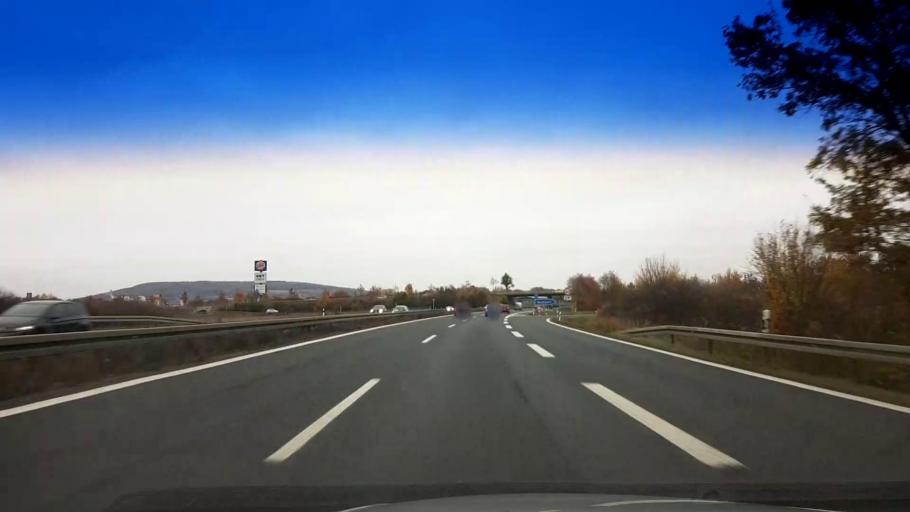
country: DE
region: Bavaria
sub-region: Upper Franconia
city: Breitengussbach
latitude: 49.9696
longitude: 10.8751
